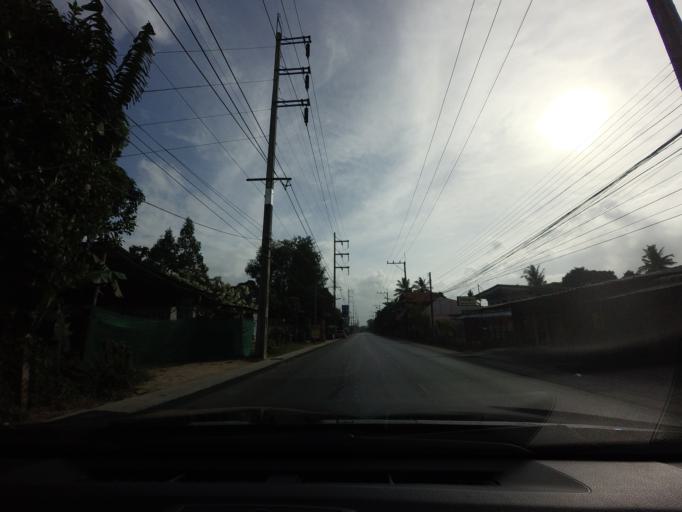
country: TH
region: Yala
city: Yala
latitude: 6.5332
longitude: 101.2629
